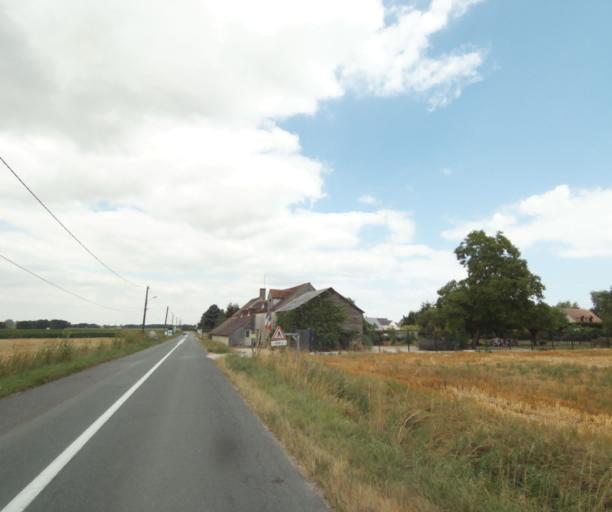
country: FR
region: Centre
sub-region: Departement du Loiret
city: Boigny-sur-Bionne
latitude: 47.9230
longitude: 2.0444
